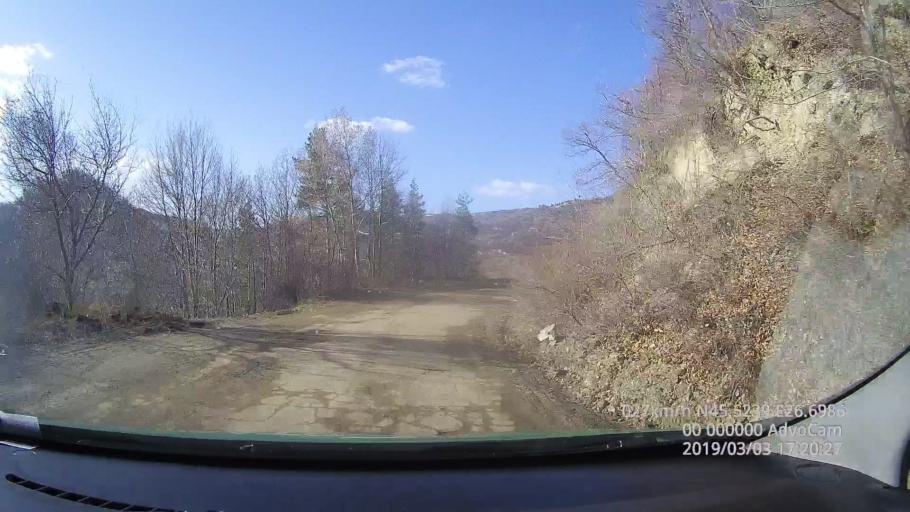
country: RO
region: Buzau
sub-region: Comuna Bisoca
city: Bisoca
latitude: 45.5240
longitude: 26.6985
